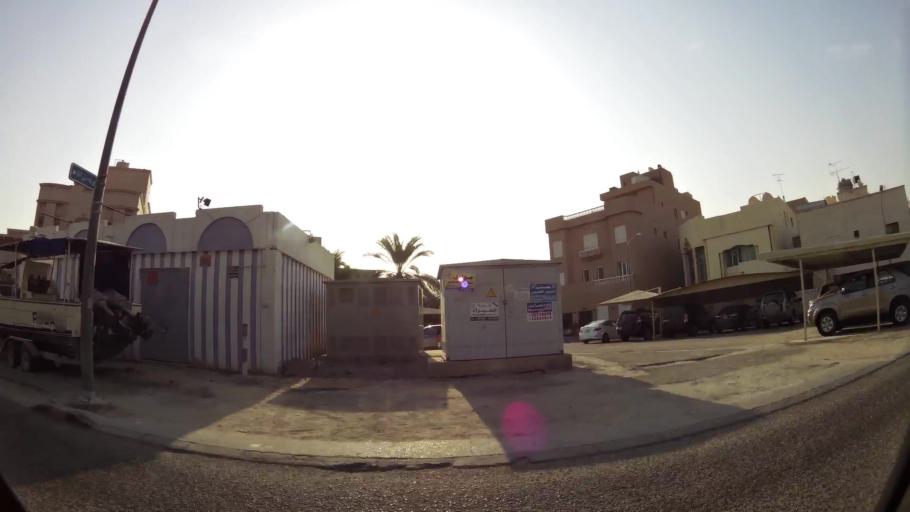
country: KW
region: Al Asimah
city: Ad Dasmah
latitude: 29.3638
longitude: 48.0077
